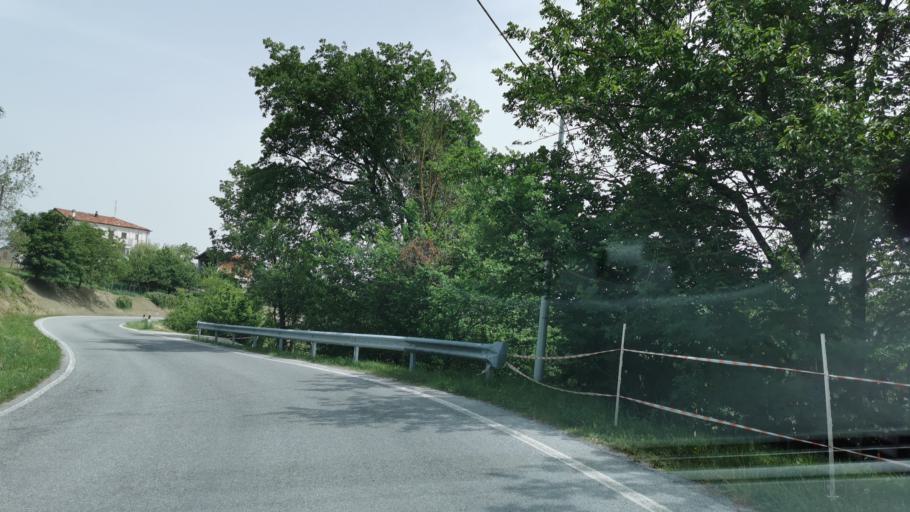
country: IT
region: Piedmont
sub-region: Provincia di Cuneo
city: Sale San Giovanni
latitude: 44.4153
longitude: 8.0851
